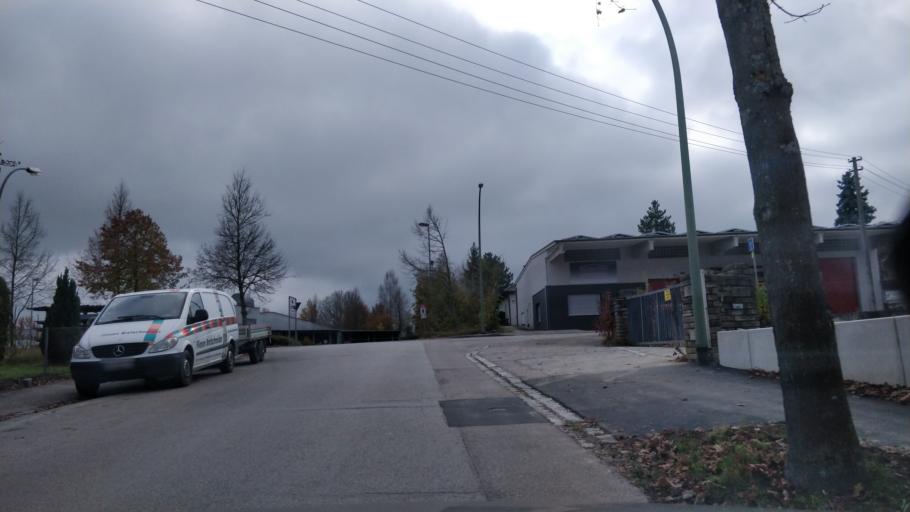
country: DE
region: Bavaria
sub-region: Swabia
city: Friedberg
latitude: 48.3493
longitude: 10.9951
